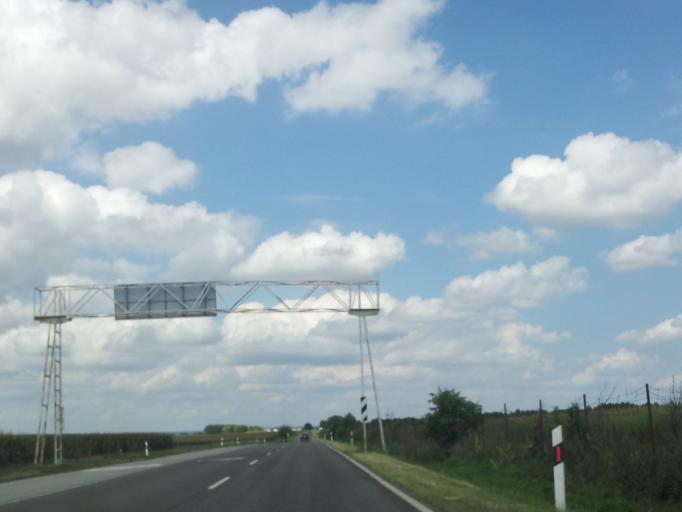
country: HU
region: Baranya
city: Mohacs
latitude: 45.9122
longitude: 18.6595
